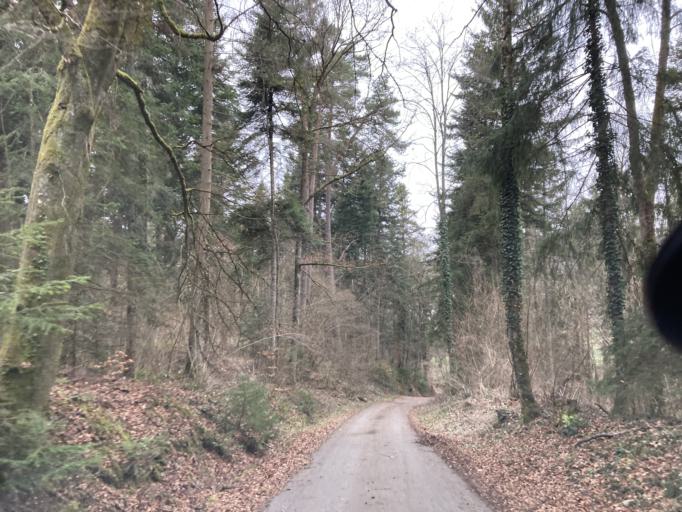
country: DE
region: Baden-Wuerttemberg
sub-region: Tuebingen Region
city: Hirrlingen
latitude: 48.4495
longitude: 8.8705
